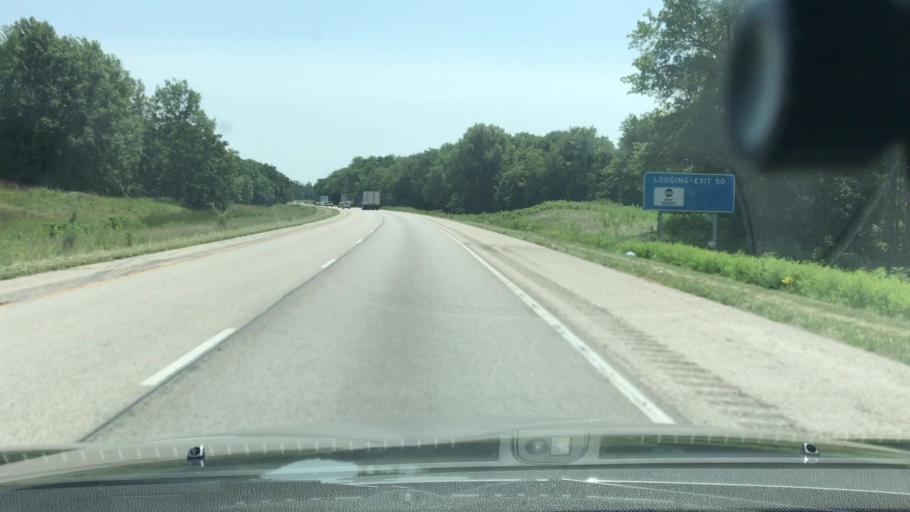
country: US
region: Illinois
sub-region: Washington County
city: Nashville
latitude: 38.4018
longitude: -89.4025
